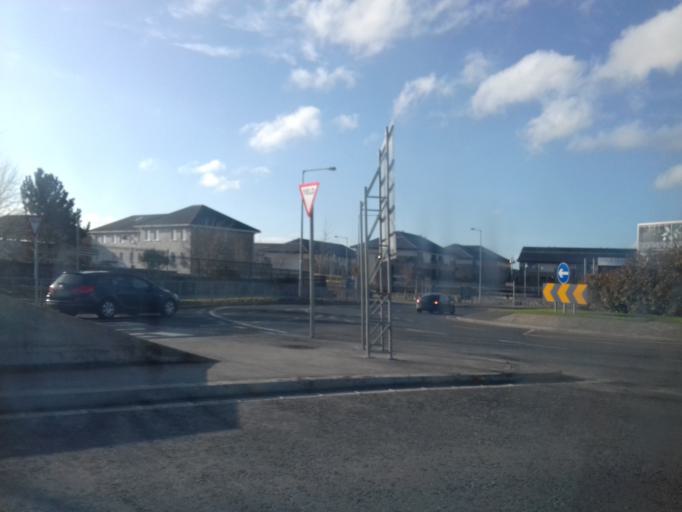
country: IE
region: Leinster
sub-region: Fingal County
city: Blanchardstown
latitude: 53.4186
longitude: -6.3816
